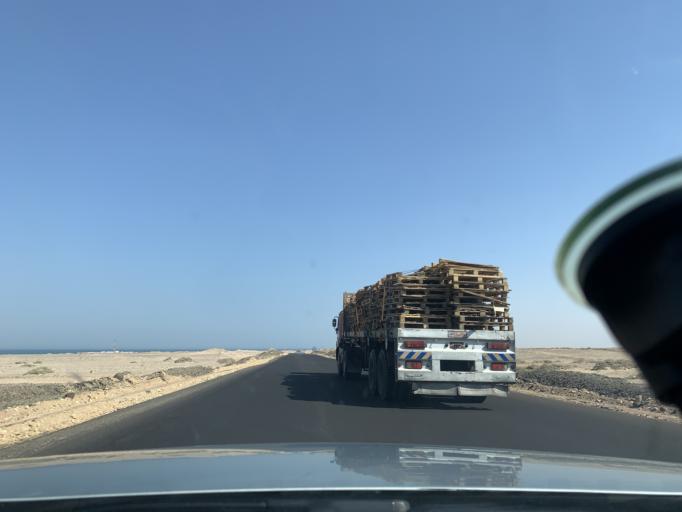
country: EG
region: South Sinai
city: Tor
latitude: 28.7300
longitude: 32.8075
